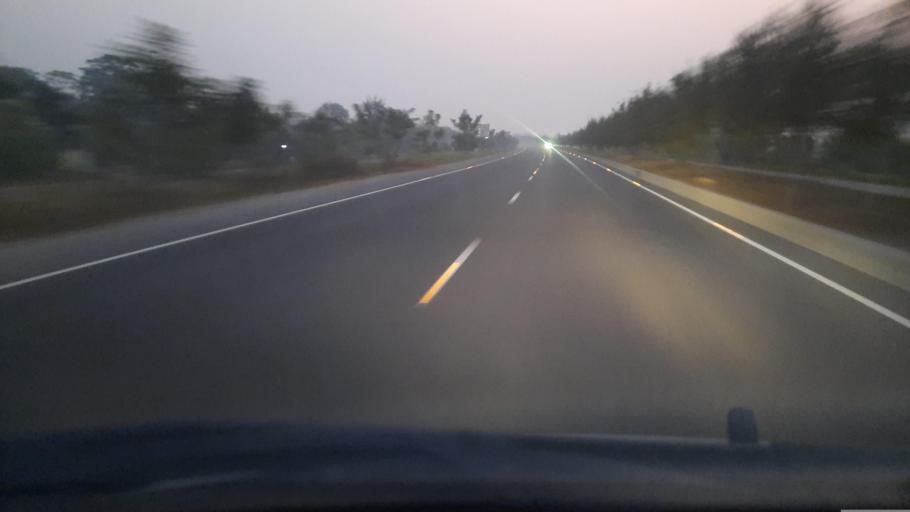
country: BD
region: Dhaka
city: Char Bhadrasan
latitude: 23.3978
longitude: 90.2351
